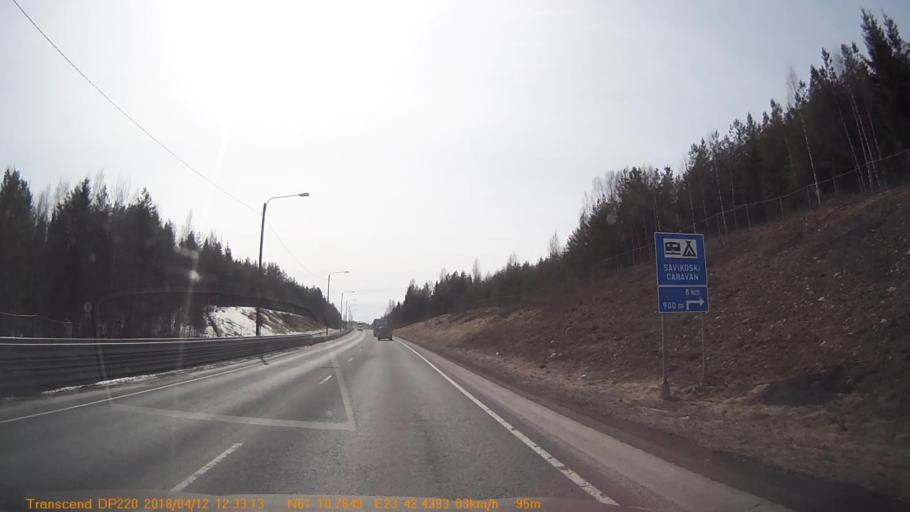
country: FI
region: Pirkanmaa
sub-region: Etelae-Pirkanmaa
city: Kylmaekoski
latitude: 61.1792
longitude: 23.7072
